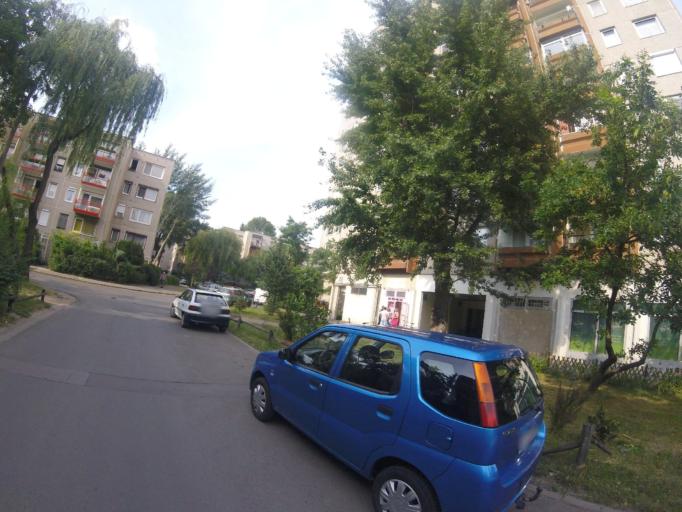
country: HU
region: Budapest
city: Budapest III. keruelet
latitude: 47.5695
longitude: 19.0520
